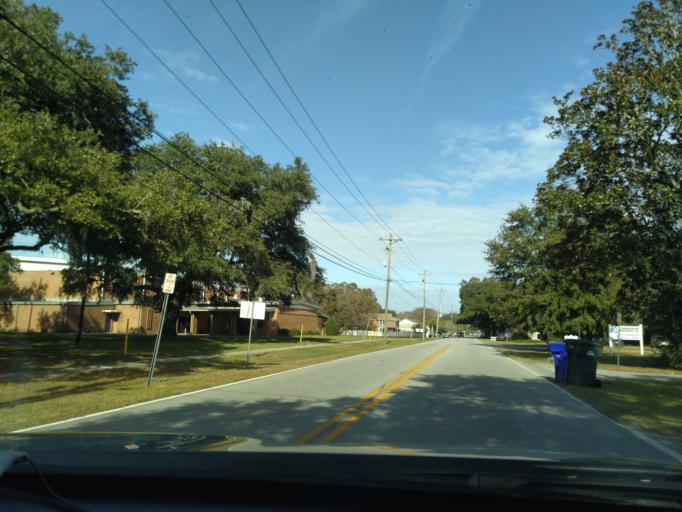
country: US
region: South Carolina
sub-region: Charleston County
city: North Charleston
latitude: 32.7907
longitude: -80.0198
